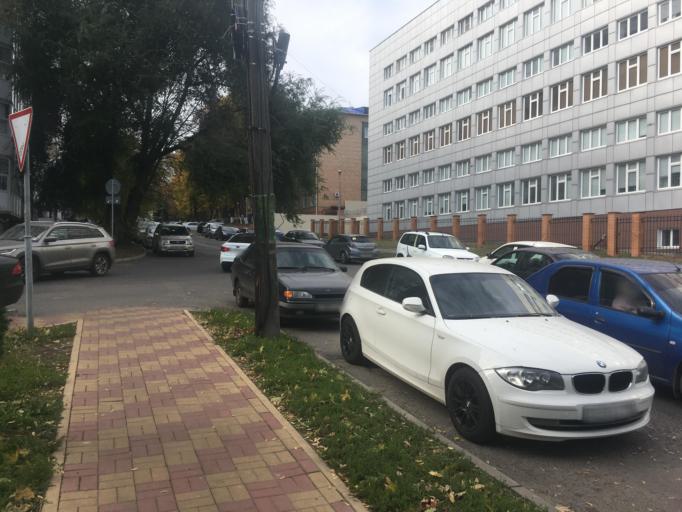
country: RU
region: Kursk
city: Kursk
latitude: 51.7457
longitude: 36.2009
